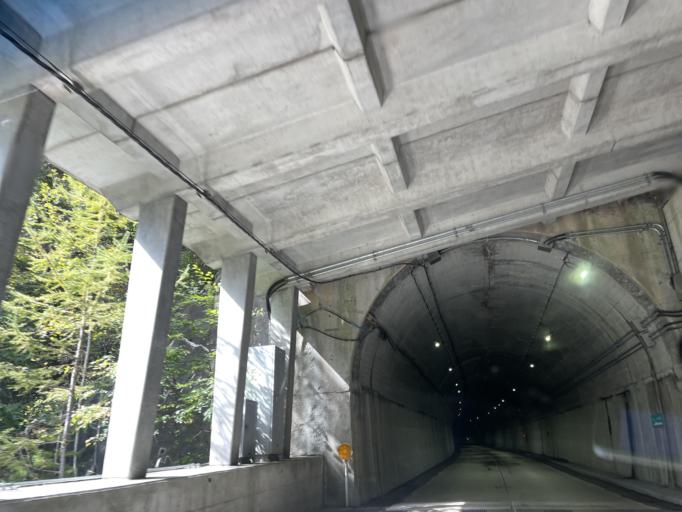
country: JP
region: Nagano
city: Omachi
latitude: 36.4917
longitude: 137.7381
